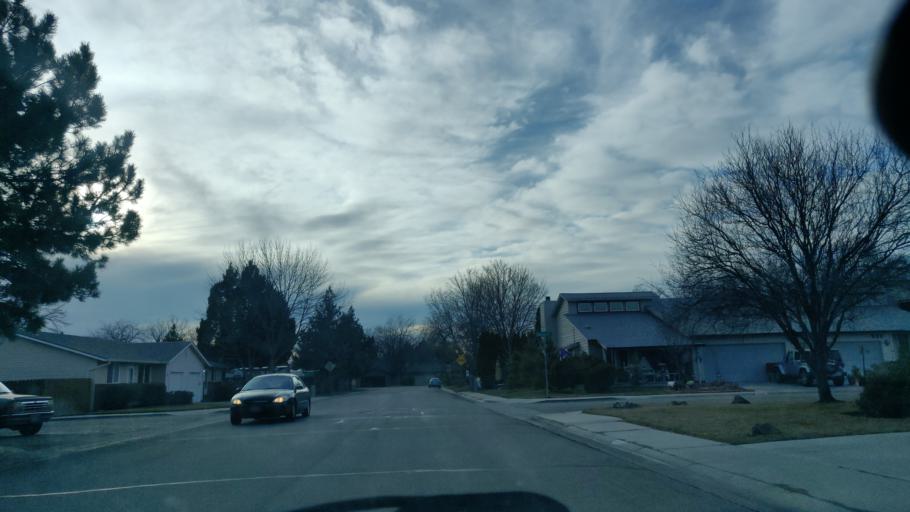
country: US
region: Idaho
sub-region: Ada County
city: Garden City
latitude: 43.6129
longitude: -116.2680
